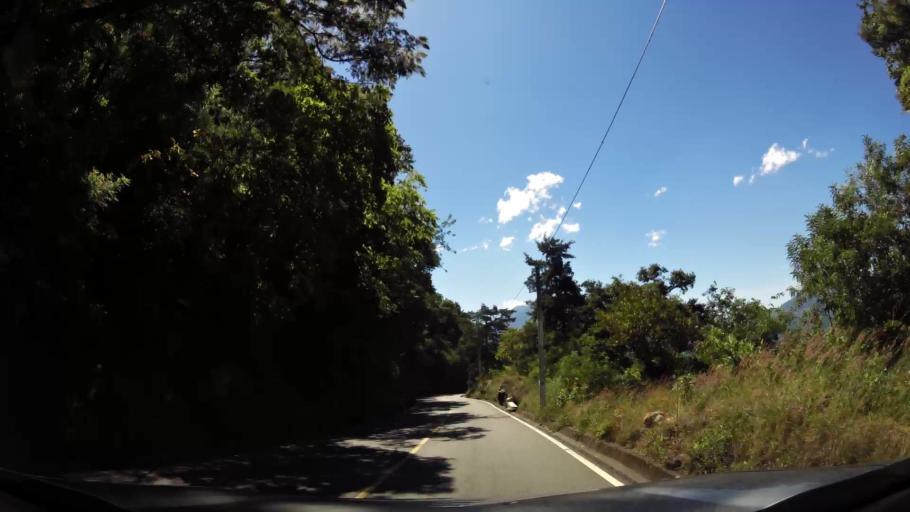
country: GT
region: Solola
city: Panajachel
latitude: 14.7458
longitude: -91.1628
